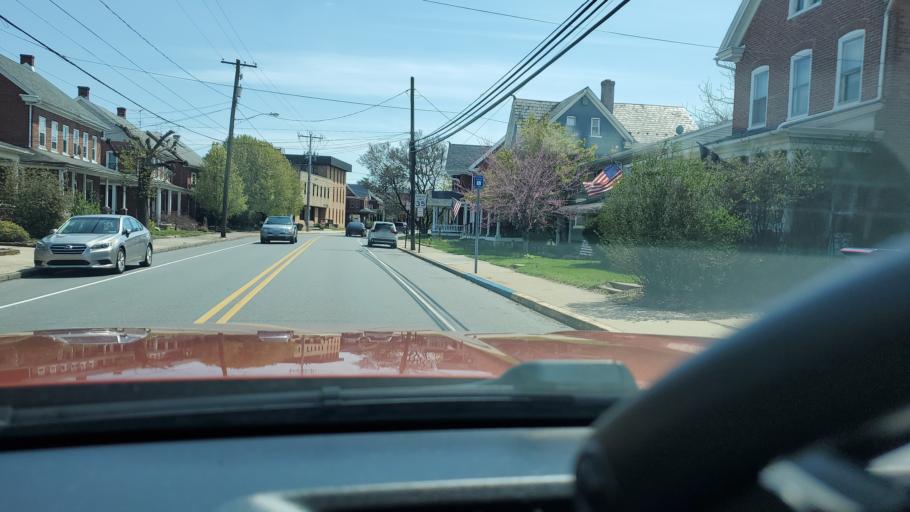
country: US
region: Pennsylvania
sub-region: Montgomery County
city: Red Hill
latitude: 40.3759
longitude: -75.4824
